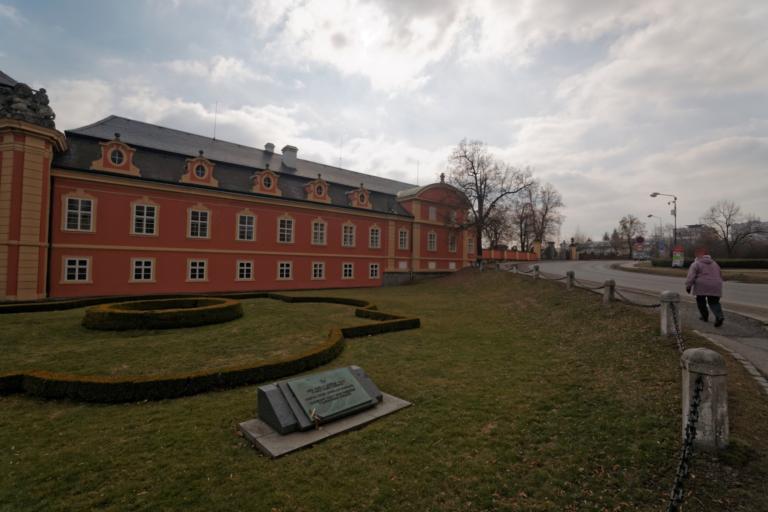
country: CZ
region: Central Bohemia
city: Dobris
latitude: 49.7822
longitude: 14.1785
